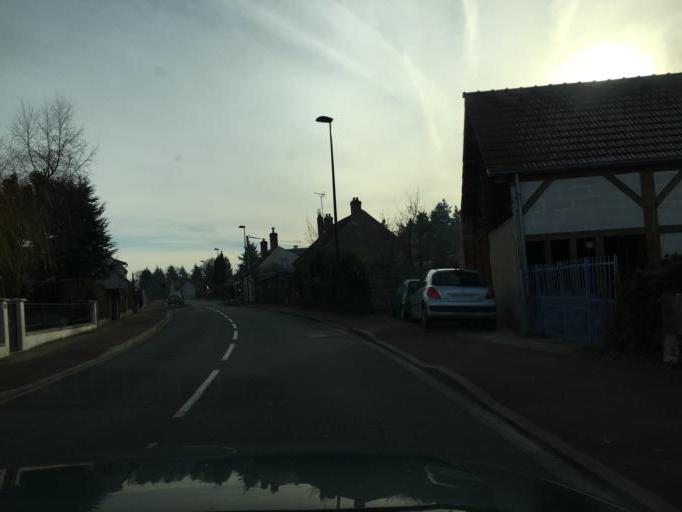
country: FR
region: Centre
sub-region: Departement du Loiret
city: Saint-Cyr-en-Val
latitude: 47.8294
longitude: 1.9698
